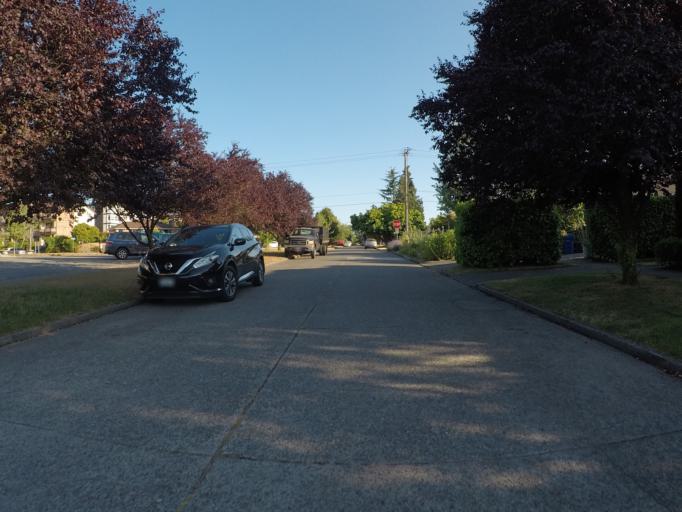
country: US
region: Washington
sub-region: King County
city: Seattle
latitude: 47.5858
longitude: -122.3877
